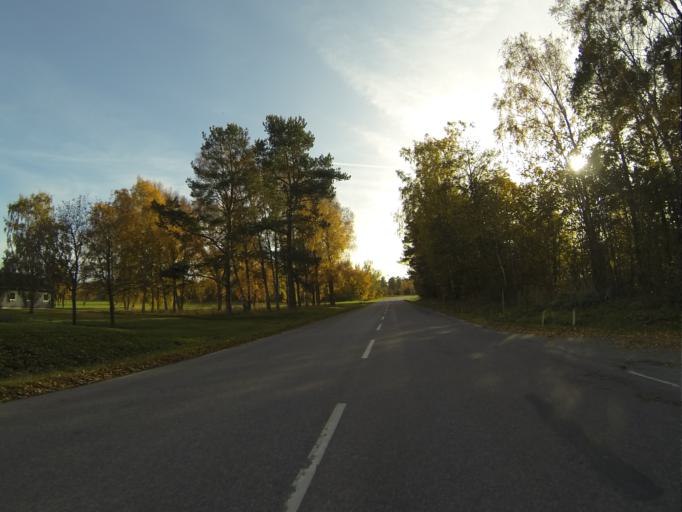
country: SE
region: Skane
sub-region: Hoors Kommun
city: Loberod
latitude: 55.7251
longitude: 13.4653
